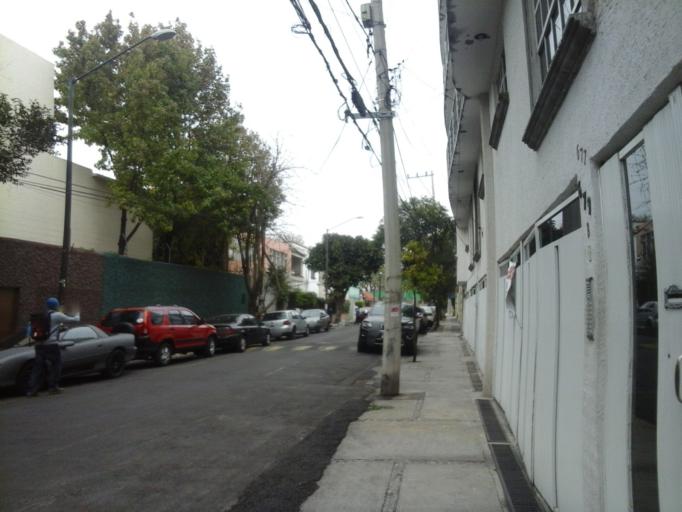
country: MX
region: Mexico
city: Colonia Lindavista
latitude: 19.4885
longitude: -99.1301
